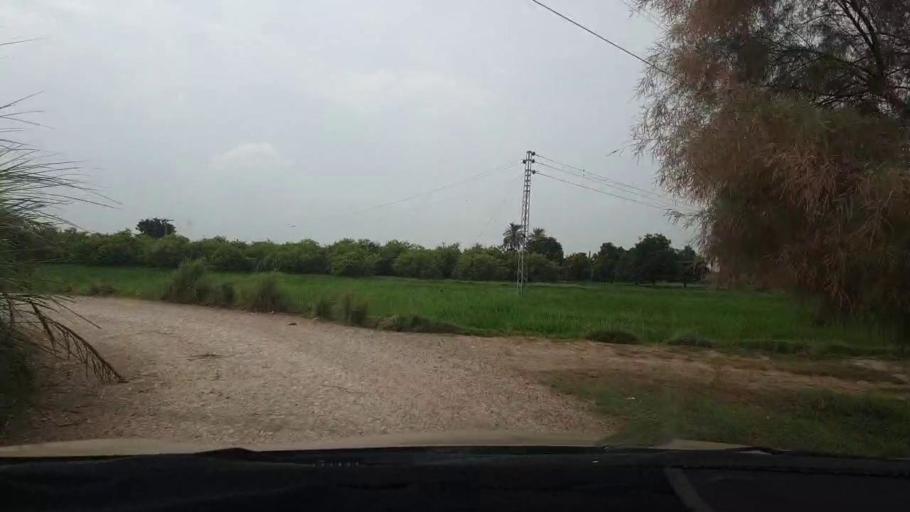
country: PK
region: Sindh
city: Naudero
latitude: 27.6345
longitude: 68.3079
